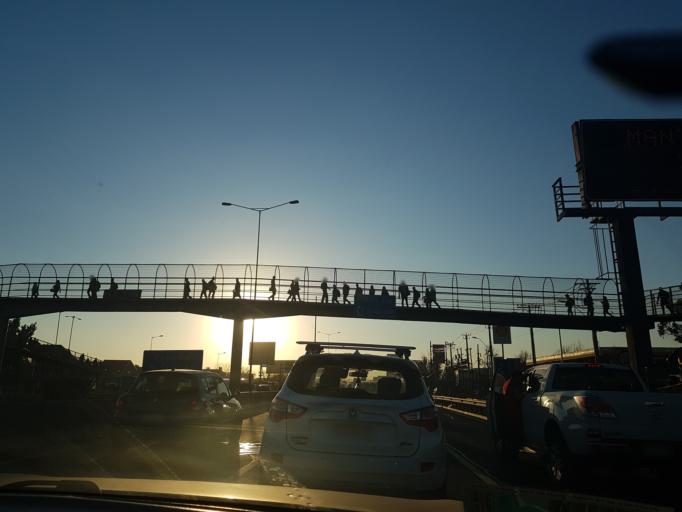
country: CL
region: Santiago Metropolitan
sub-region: Provincia de Santiago
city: Santiago
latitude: -33.3810
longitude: -70.6449
